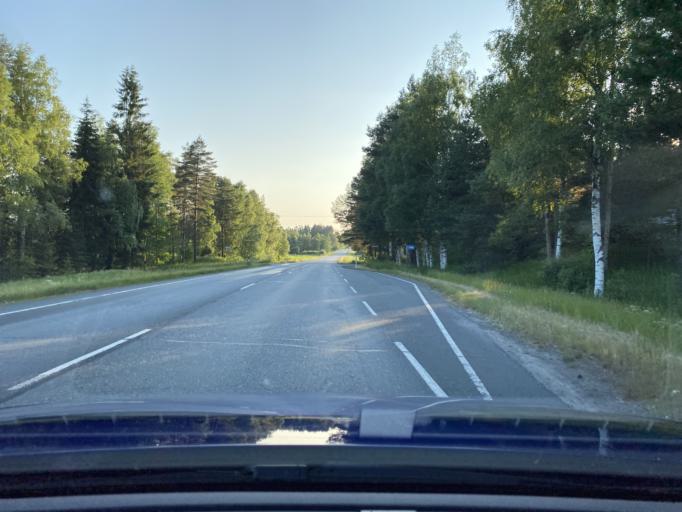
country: FI
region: Haeme
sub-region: Forssa
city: Tammela
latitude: 60.8254
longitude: 23.9767
